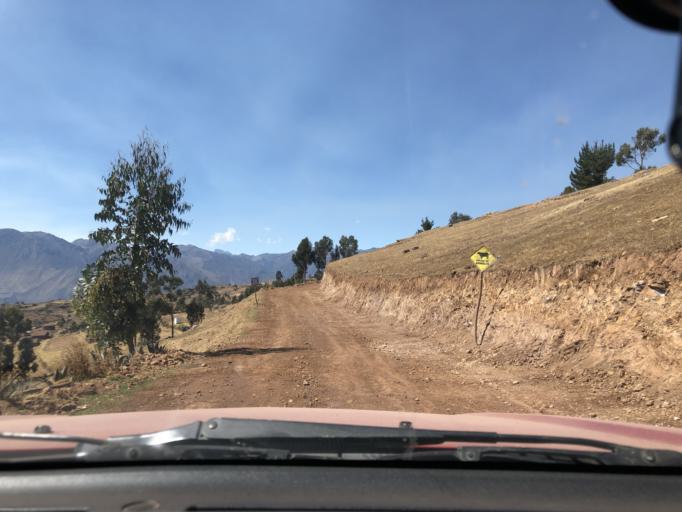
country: PE
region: Ayacucho
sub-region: Provincia de La Mar
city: Chilcas
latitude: -13.1685
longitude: -73.8574
